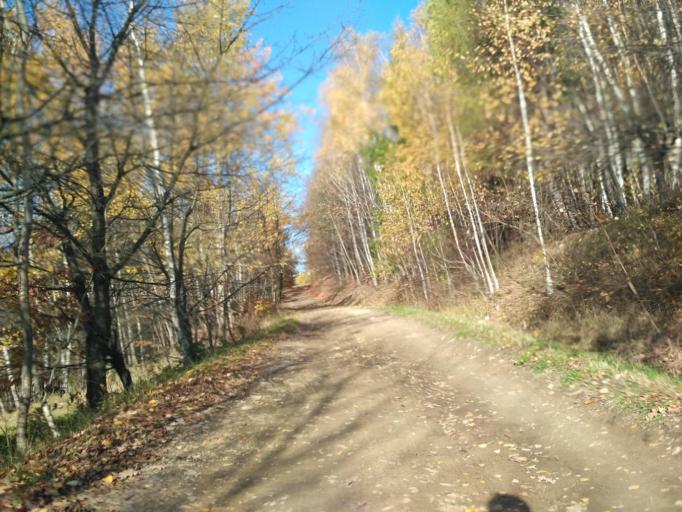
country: PL
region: Subcarpathian Voivodeship
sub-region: Powiat rzeszowski
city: Blazowa
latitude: 49.8619
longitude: 22.0863
